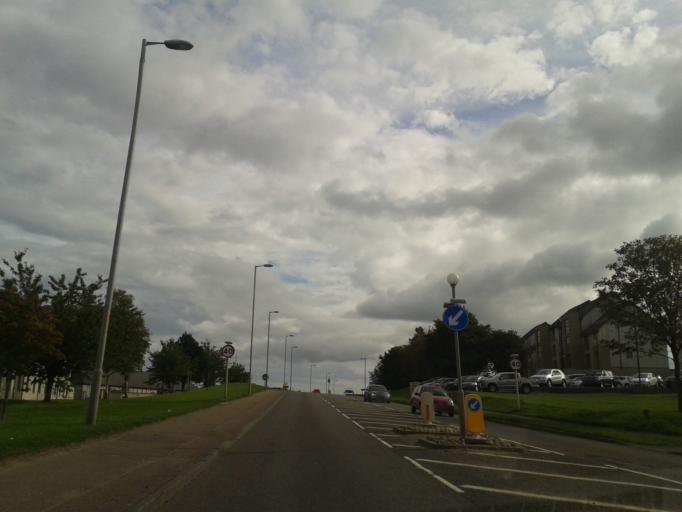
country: GB
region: Scotland
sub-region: Moray
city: Elgin
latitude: 57.6468
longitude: -3.2896
